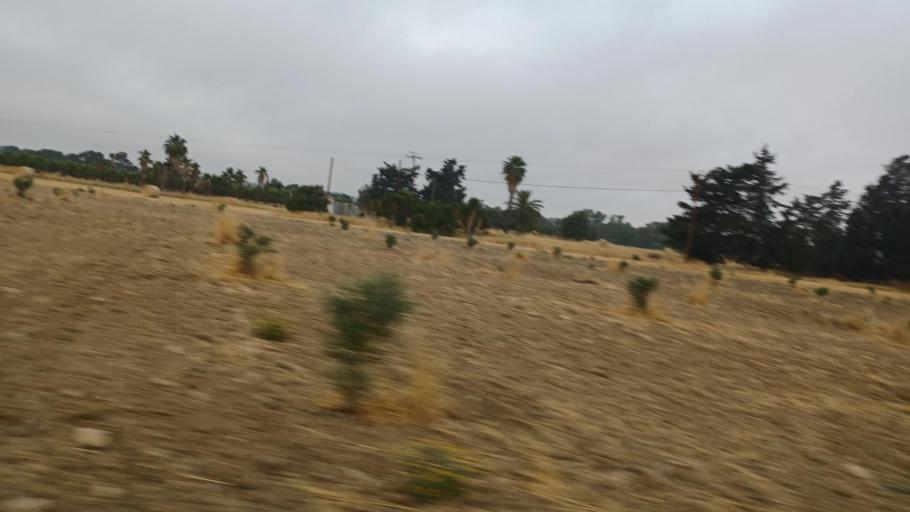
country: CY
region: Larnaka
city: Tersefanou
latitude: 34.8328
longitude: 33.5099
